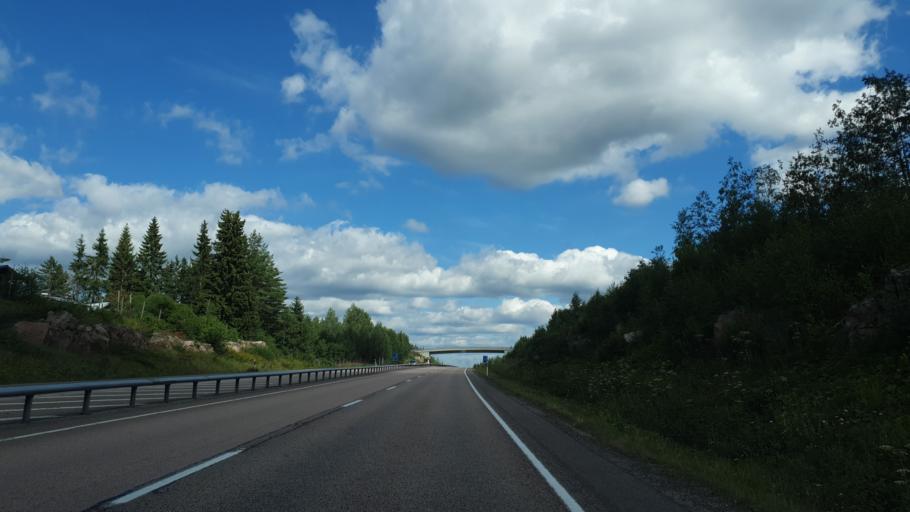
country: FI
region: Central Finland
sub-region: Jaemsae
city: Jaemsae
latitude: 61.7865
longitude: 24.9200
